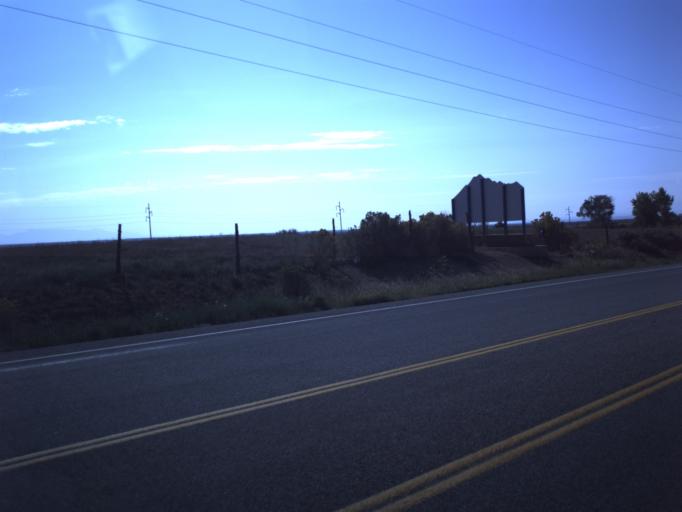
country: US
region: Utah
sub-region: San Juan County
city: Blanding
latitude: 37.5946
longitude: -109.4785
